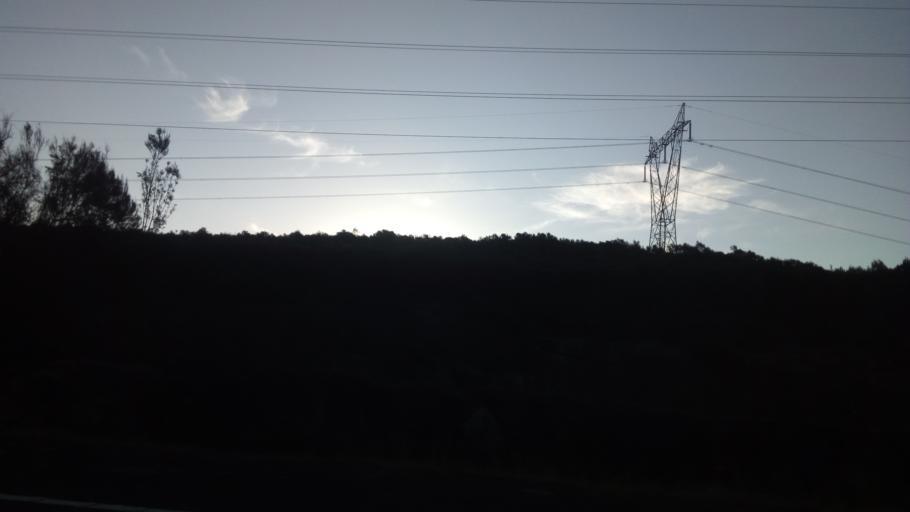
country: AU
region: New South Wales
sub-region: Wollongong
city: Helensburgh
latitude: -34.1883
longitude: 150.9685
